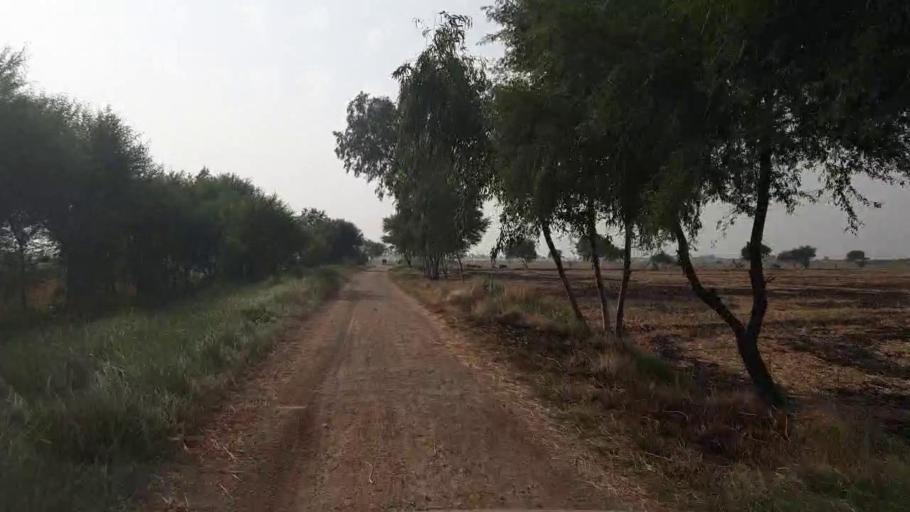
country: PK
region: Sindh
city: Tando Muhammad Khan
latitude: 25.1036
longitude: 68.5016
